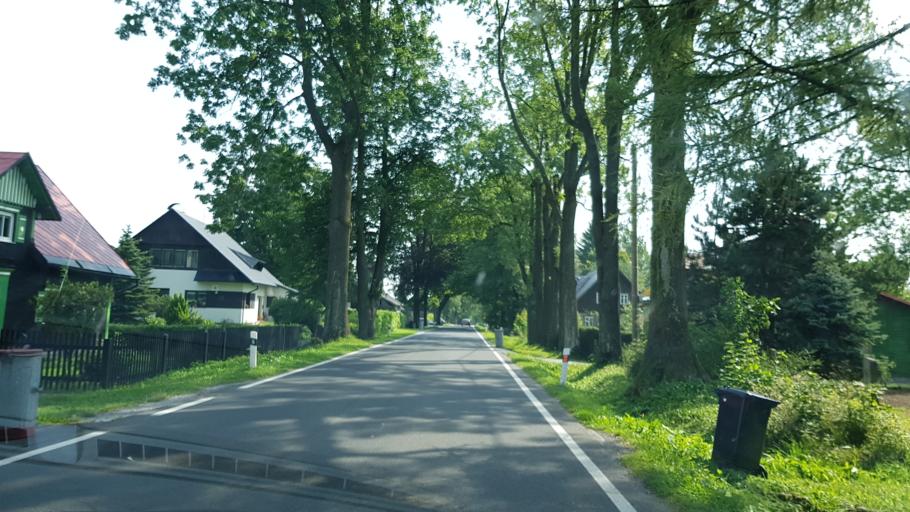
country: CZ
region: Olomoucky
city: Pisecna
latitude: 50.2295
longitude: 17.2993
